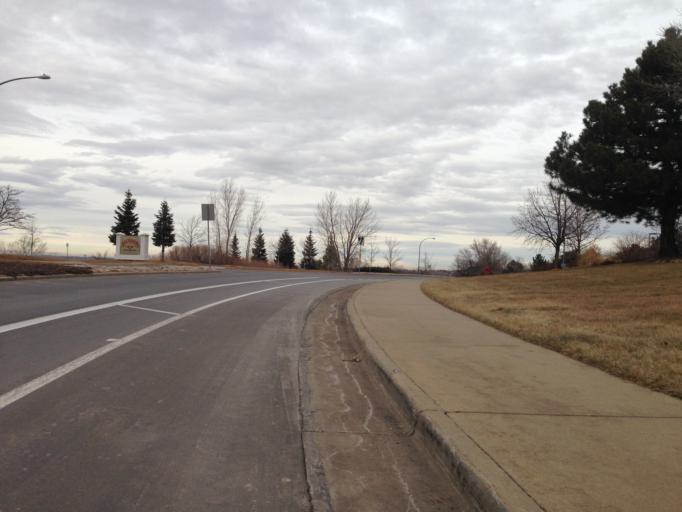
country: US
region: Colorado
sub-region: Adams County
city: Westminster
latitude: 39.8606
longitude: -105.0512
